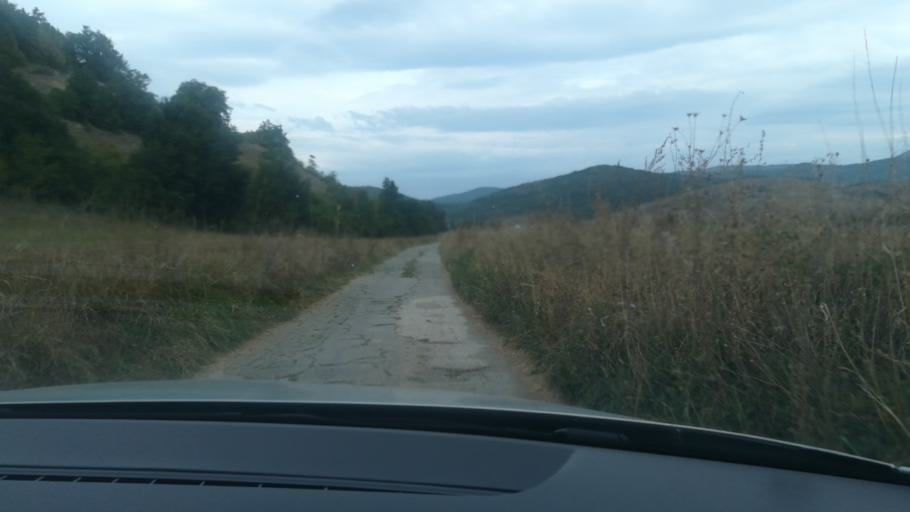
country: MK
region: Debarca
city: Belcista
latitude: 41.2889
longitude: 20.8304
